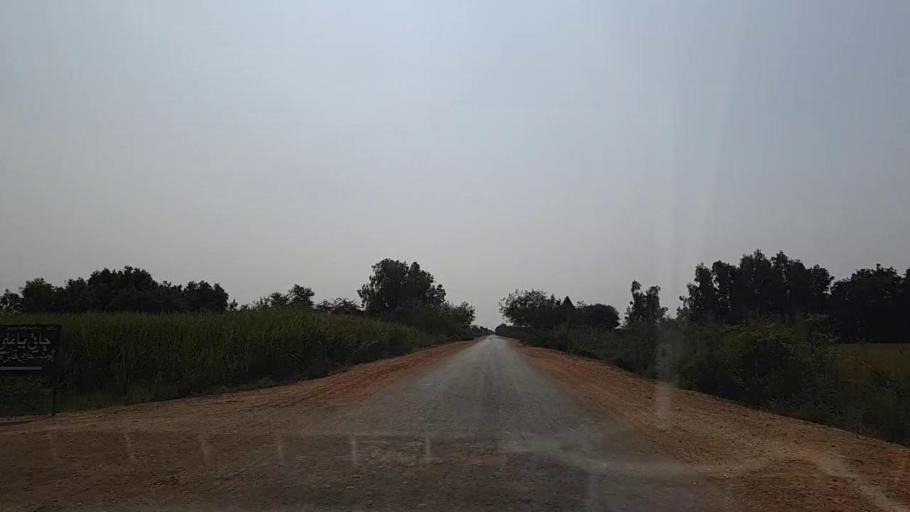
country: PK
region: Sindh
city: Chuhar Jamali
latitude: 24.2623
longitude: 67.9085
